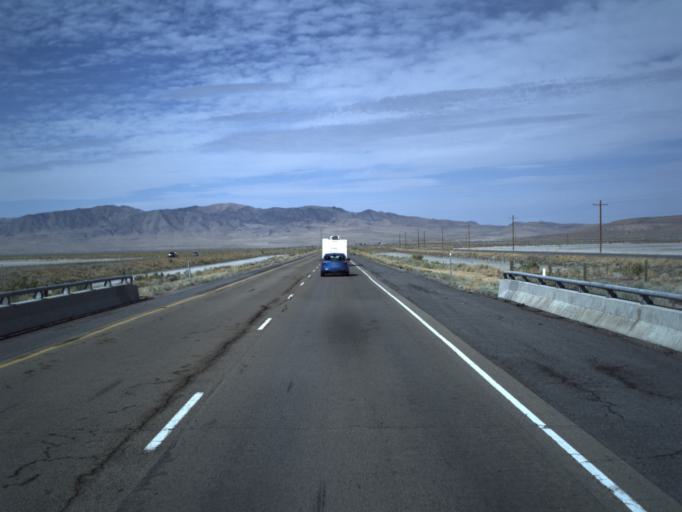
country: US
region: Utah
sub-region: Tooele County
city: Grantsville
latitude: 40.7530
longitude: -112.7218
